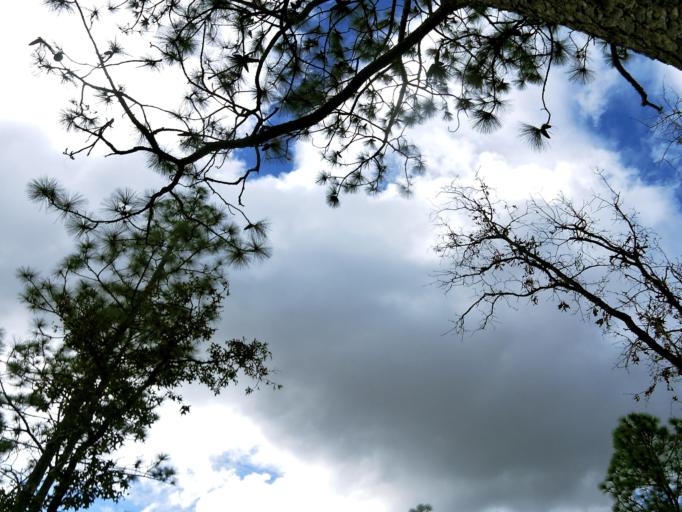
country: US
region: Florida
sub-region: Clay County
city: Keystone Heights
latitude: 29.8356
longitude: -81.9663
